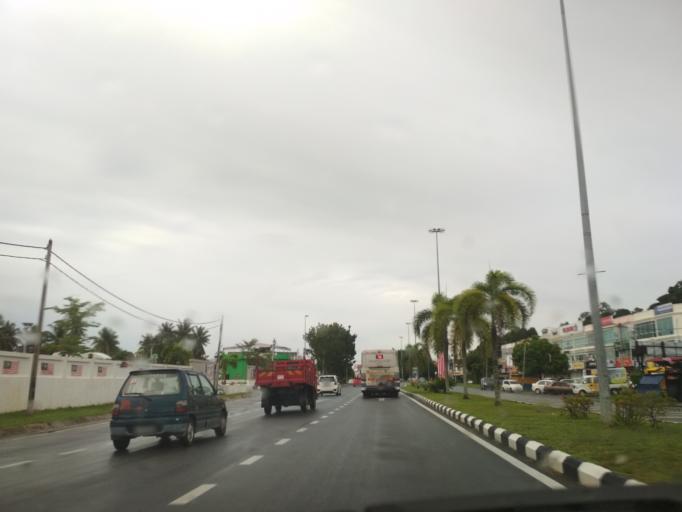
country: MY
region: Perlis
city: Kangar
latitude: 6.4328
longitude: 100.1866
